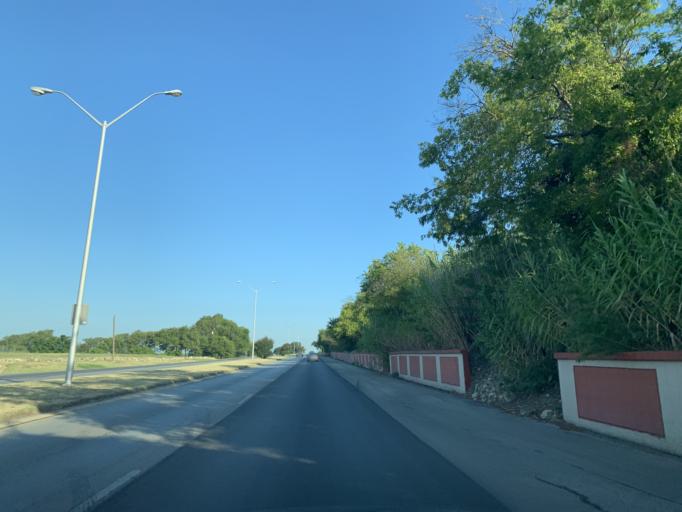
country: US
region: Texas
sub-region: Tarrant County
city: River Oaks
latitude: 32.7720
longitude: -97.3622
